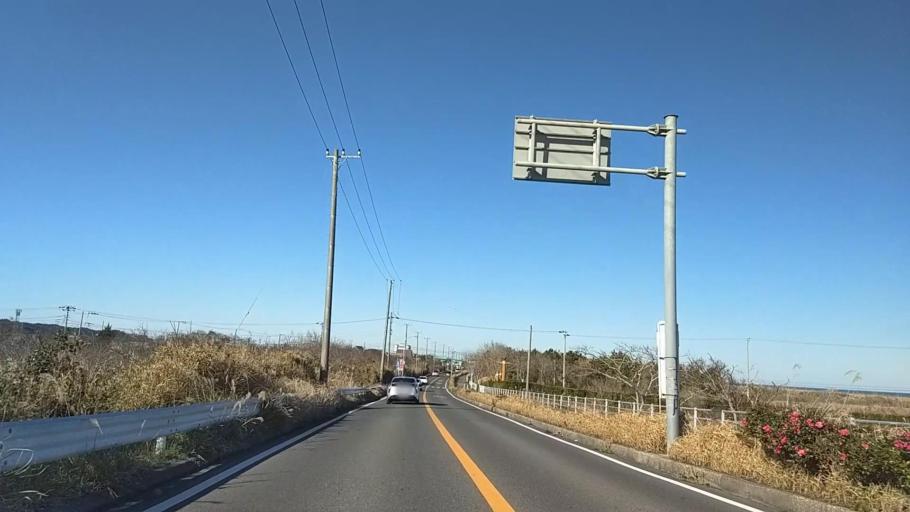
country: JP
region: Chiba
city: Ohara
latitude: 35.3344
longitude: 140.3921
